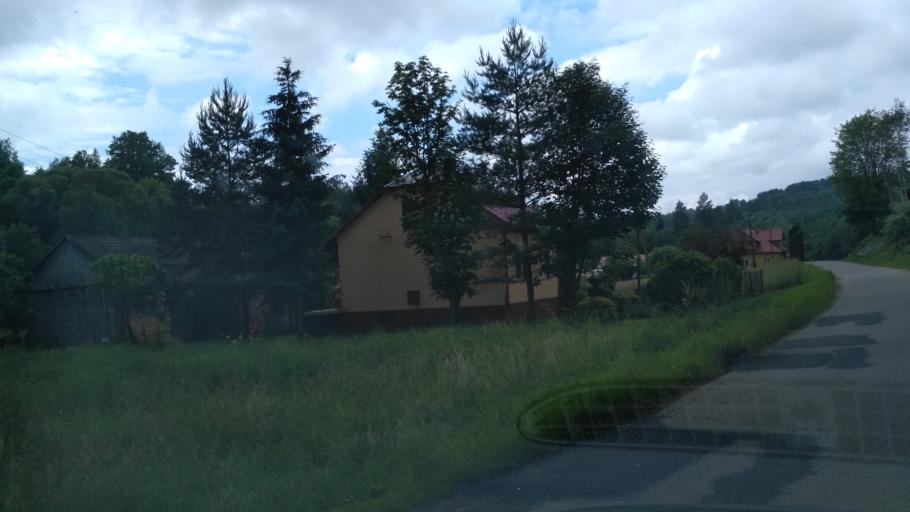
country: PL
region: Subcarpathian Voivodeship
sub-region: Powiat przemyski
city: Dubiecko
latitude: 49.8394
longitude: 22.4052
